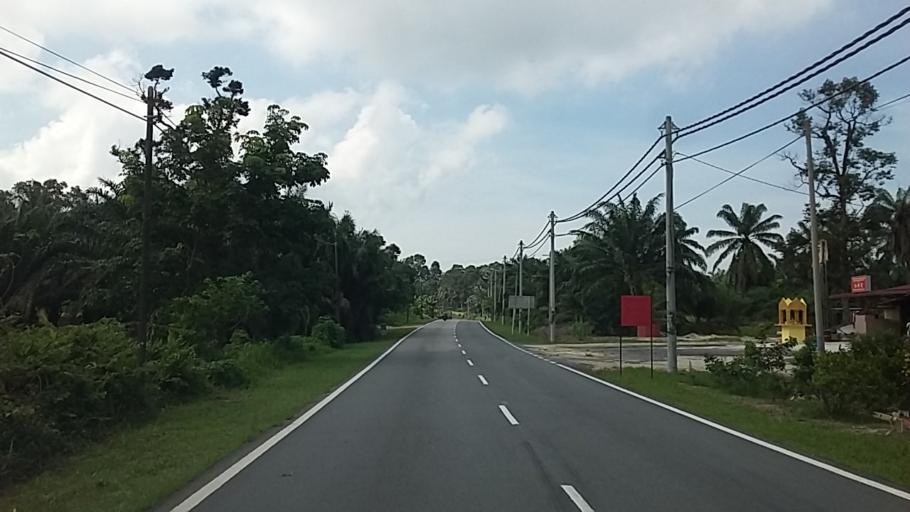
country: MY
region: Johor
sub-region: Daerah Batu Pahat
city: Batu Pahat
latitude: 1.7906
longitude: 102.8978
